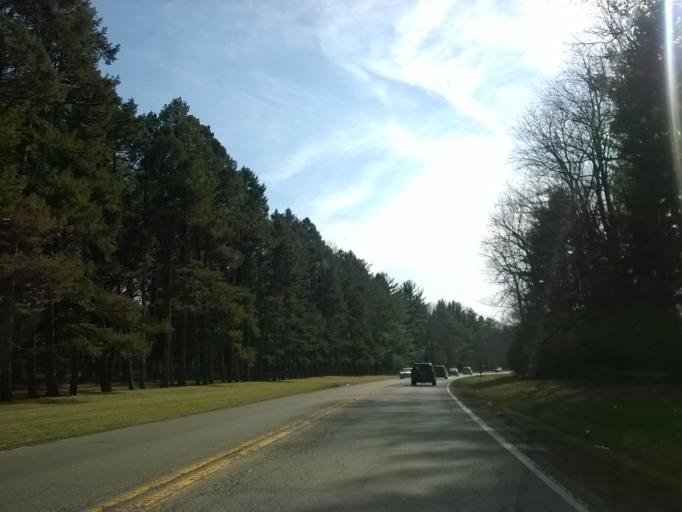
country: US
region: Indiana
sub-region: Marion County
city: Broad Ripple
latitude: 39.8609
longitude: -86.1712
